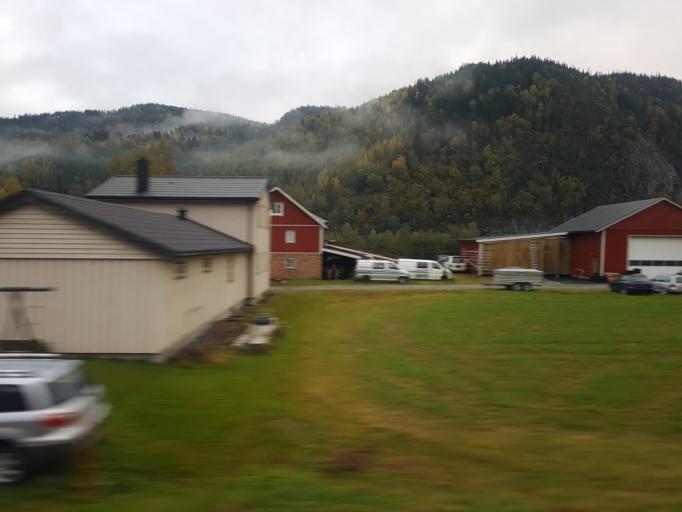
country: NO
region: Sor-Trondelag
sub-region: Melhus
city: Lundamo
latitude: 63.1020
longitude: 10.2340
